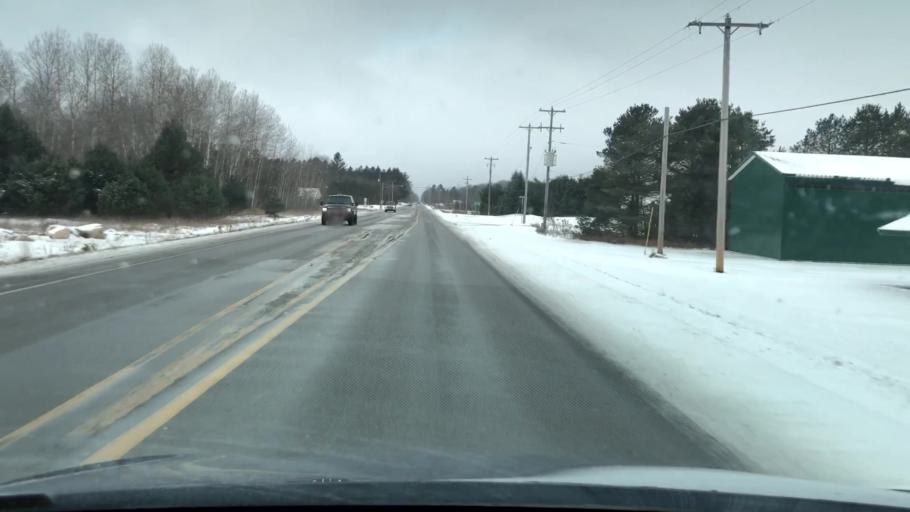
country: US
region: Michigan
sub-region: Wexford County
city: Cadillac
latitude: 44.2812
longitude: -85.4544
